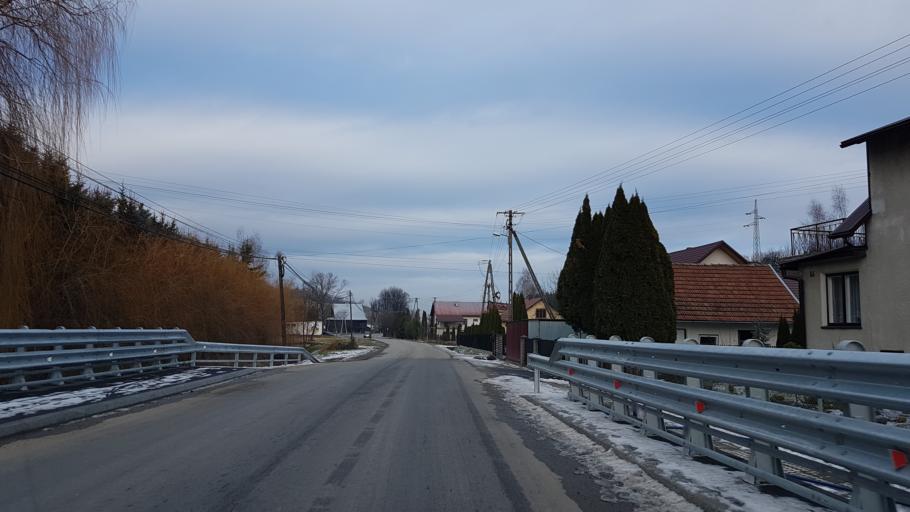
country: PL
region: Lesser Poland Voivodeship
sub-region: Powiat nowosadecki
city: Stary Sacz
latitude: 49.5414
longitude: 20.6131
